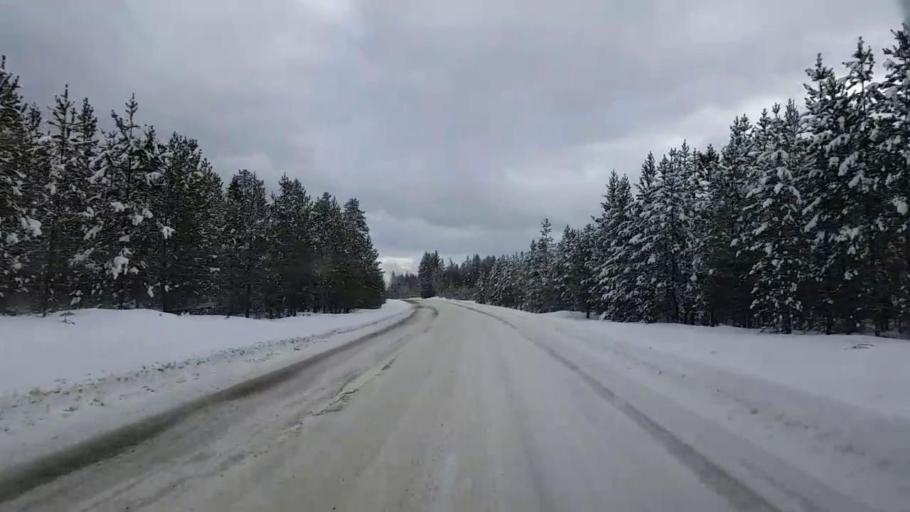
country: SE
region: Jaemtland
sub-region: Harjedalens Kommun
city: Sveg
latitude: 62.1172
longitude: 15.0435
